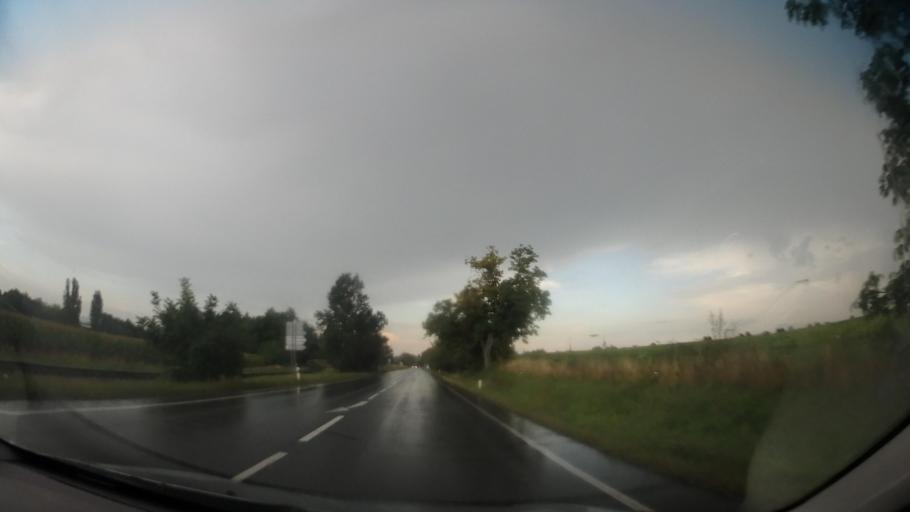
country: CZ
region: Olomoucky
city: Litovel
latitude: 49.6929
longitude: 17.0426
